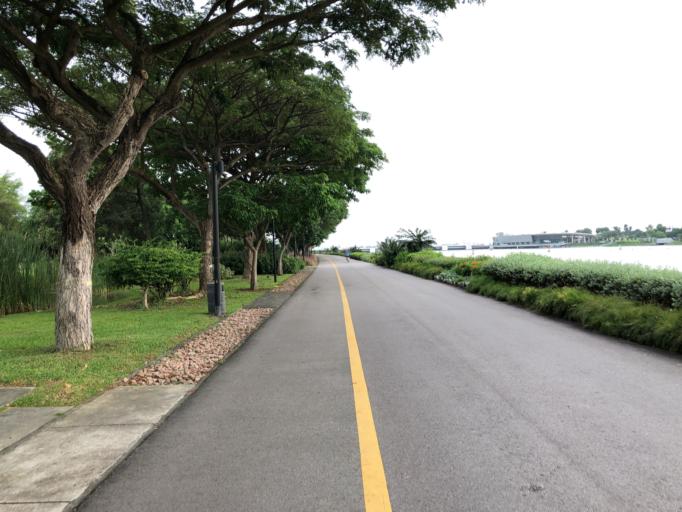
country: SG
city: Singapore
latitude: 1.2877
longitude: 103.8693
